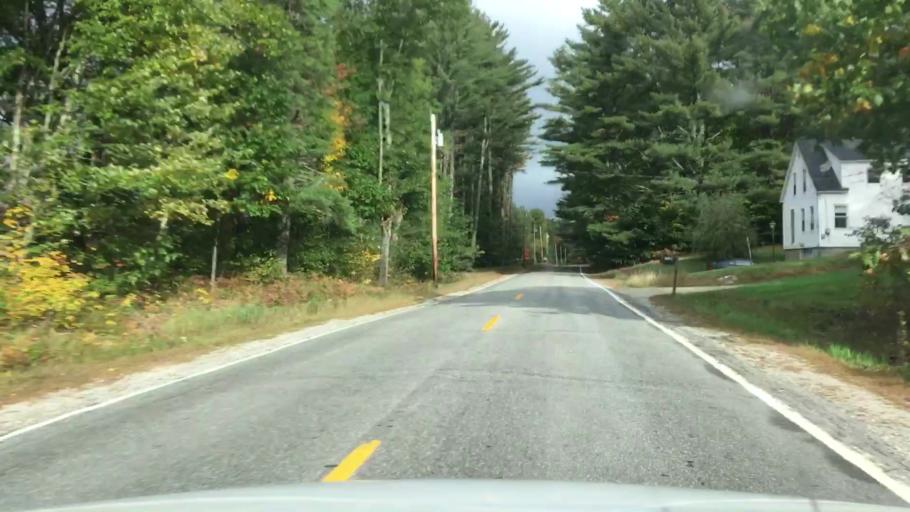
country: US
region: Maine
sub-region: Oxford County
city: Bethel
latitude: 44.3350
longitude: -70.7782
